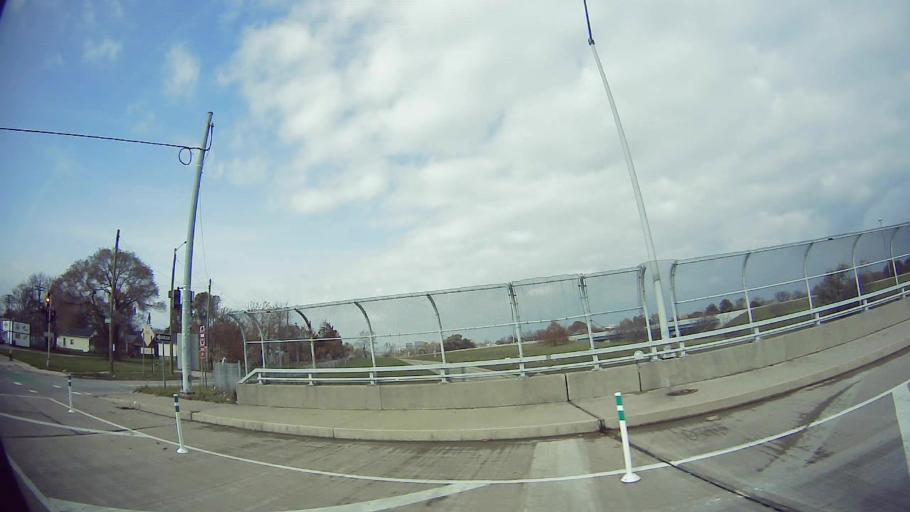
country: US
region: Michigan
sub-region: Wayne County
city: Detroit
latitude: 42.3315
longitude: -83.0873
